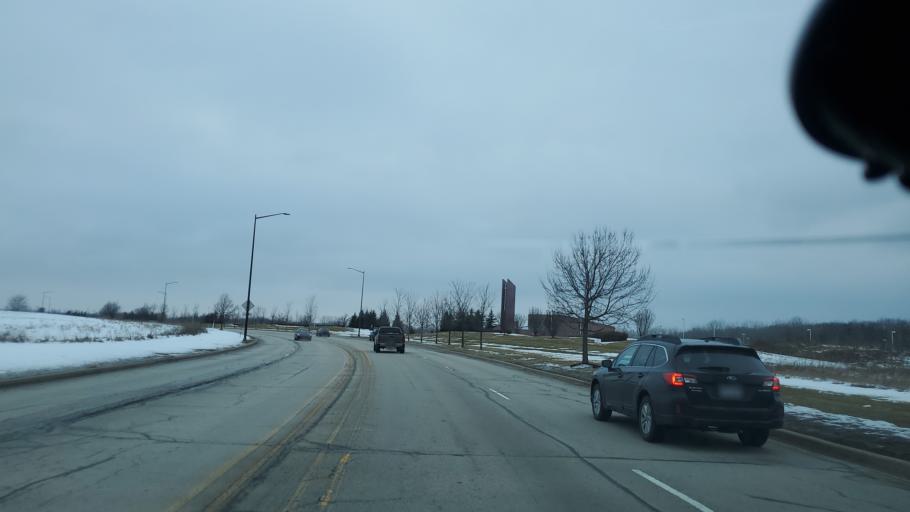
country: US
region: Illinois
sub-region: DuPage County
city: Warrenville
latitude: 41.8083
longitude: -88.2400
